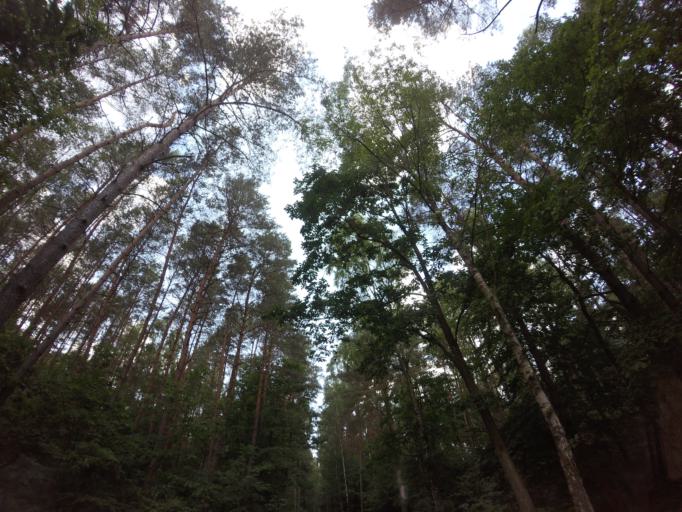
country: PL
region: West Pomeranian Voivodeship
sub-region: Powiat choszczenski
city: Bierzwnik
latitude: 53.0814
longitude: 15.6734
